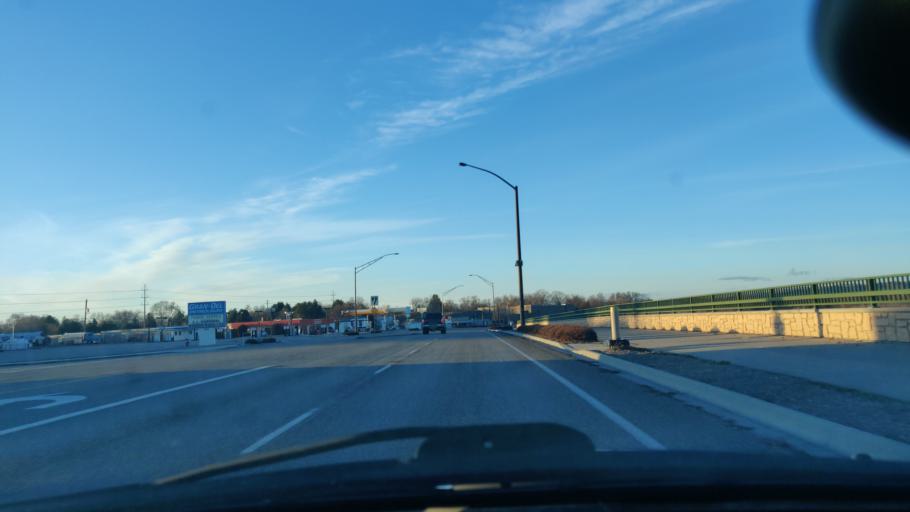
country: US
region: Idaho
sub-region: Ada County
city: Boise
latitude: 43.5772
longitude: -116.1957
